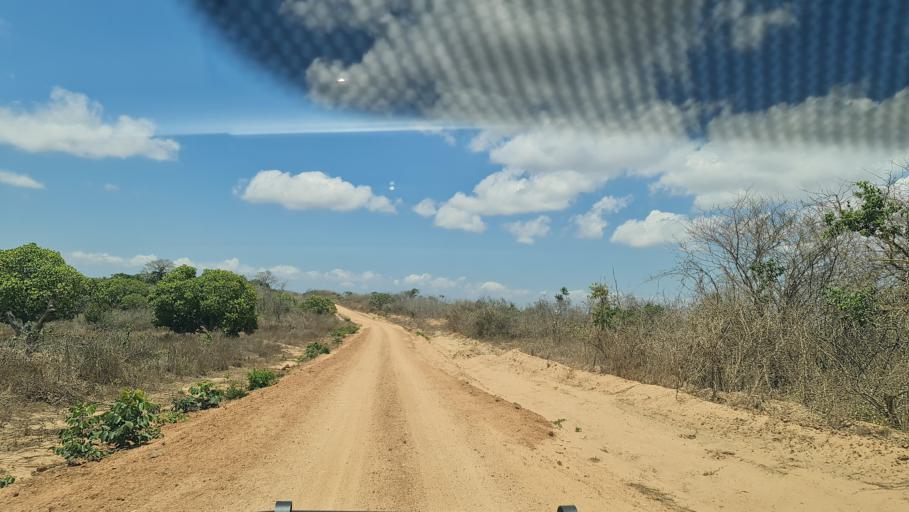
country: MZ
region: Nampula
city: Nacala
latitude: -14.3230
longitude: 40.5872
